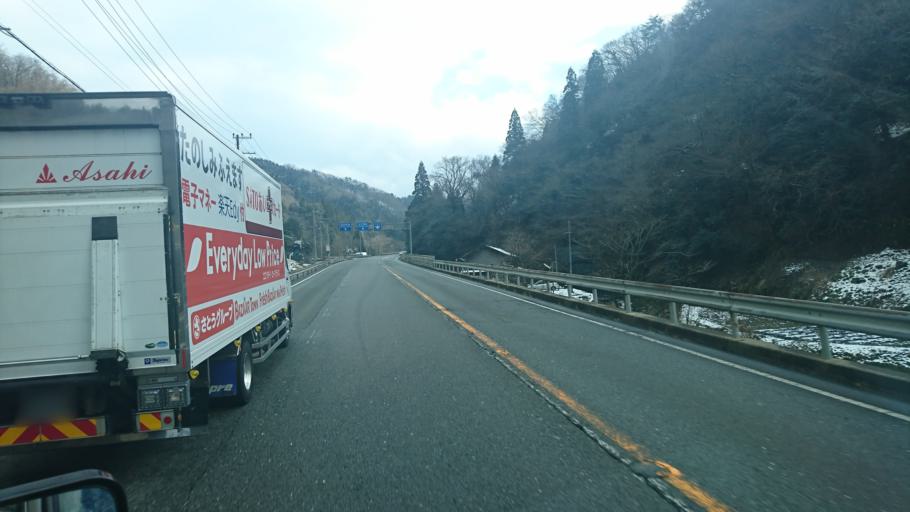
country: JP
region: Tottori
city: Tottori
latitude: 35.5233
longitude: 134.5213
